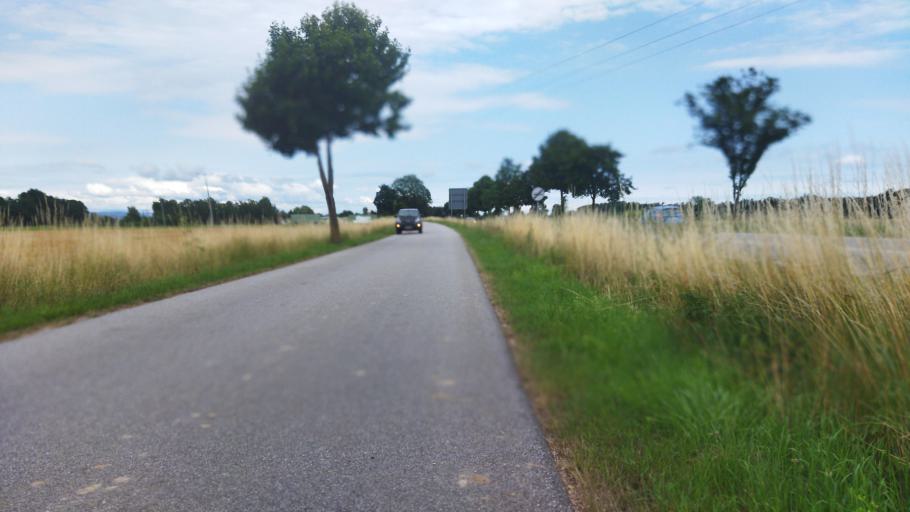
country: DE
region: Bavaria
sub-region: Upper Palatinate
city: Mintraching
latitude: 48.9764
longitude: 12.2902
